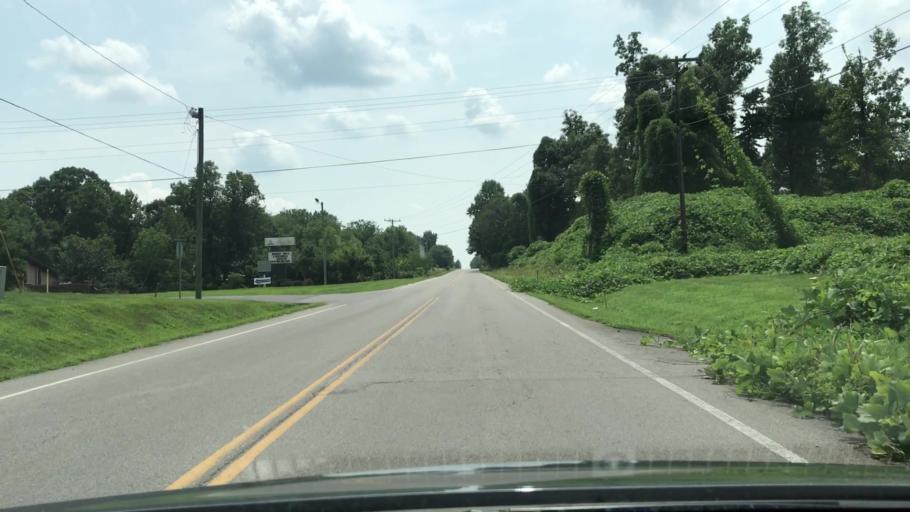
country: US
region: Tennessee
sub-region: Sumner County
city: Portland
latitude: 36.5219
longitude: -86.5016
